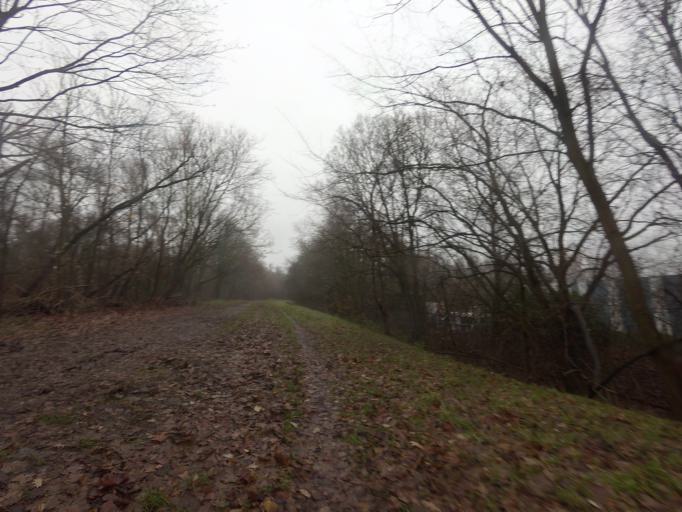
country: BE
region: Flanders
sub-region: Provincie Antwerpen
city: Hoboken
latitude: 51.1835
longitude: 4.3345
